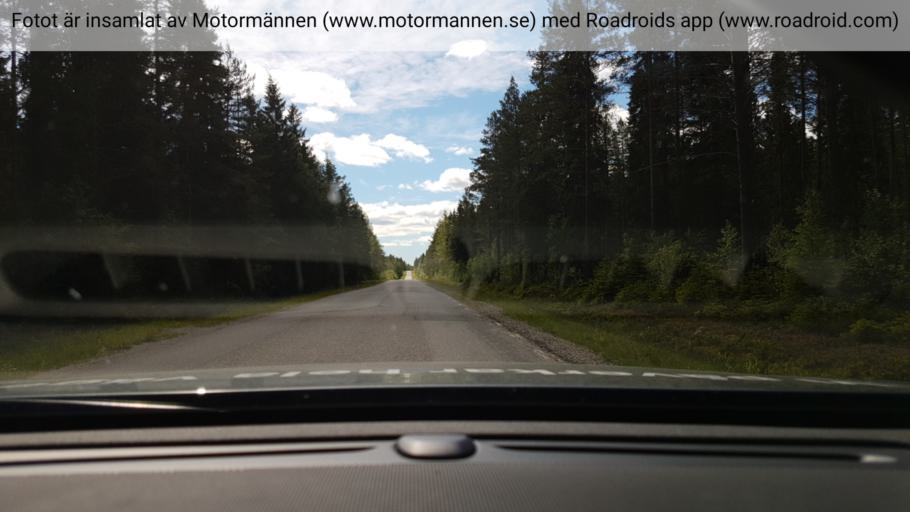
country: SE
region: Vaesterbotten
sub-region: Skelleftea Kommun
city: Burea
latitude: 64.4331
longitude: 21.3538
